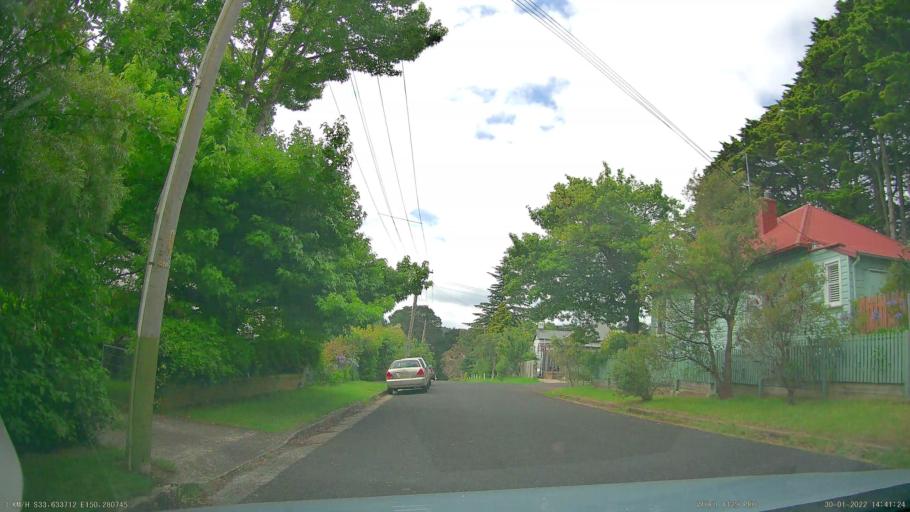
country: AU
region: New South Wales
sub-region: Blue Mountains Municipality
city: Blackheath
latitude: -33.6336
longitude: 150.2807
